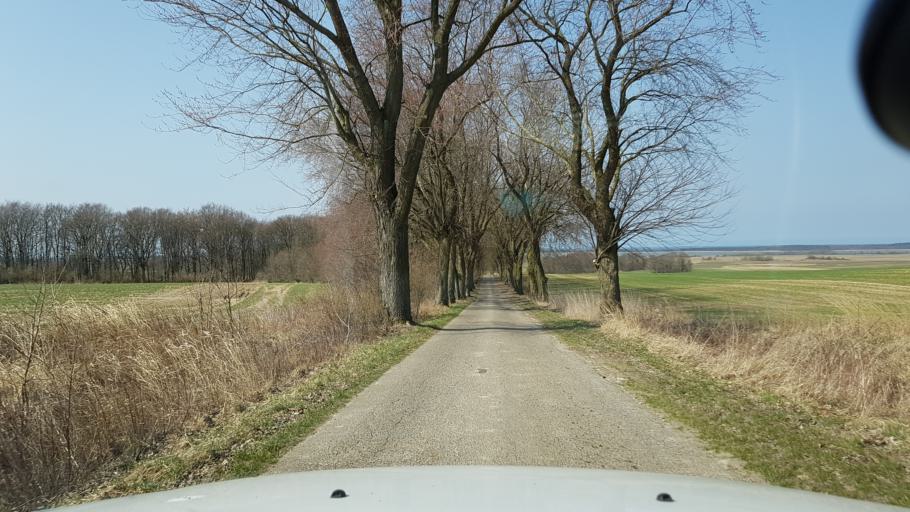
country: PL
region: West Pomeranian Voivodeship
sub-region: Powiat slawienski
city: Darlowo
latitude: 54.4656
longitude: 16.4990
